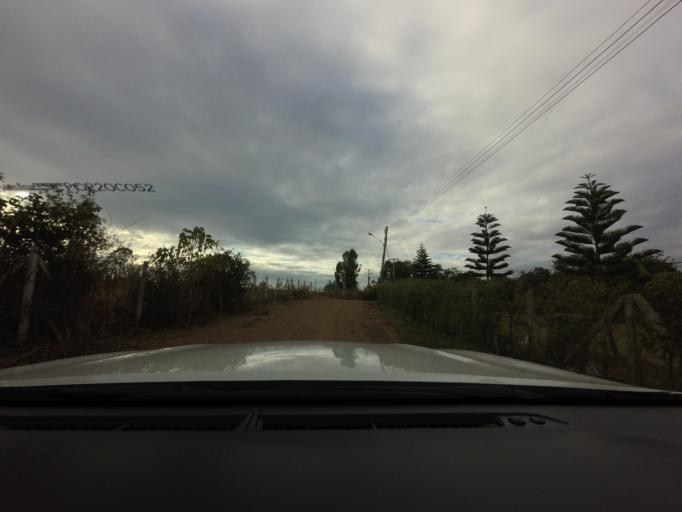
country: TH
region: Nakhon Ratchasima
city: Wang Nam Khiao
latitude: 14.4762
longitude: 101.6563
